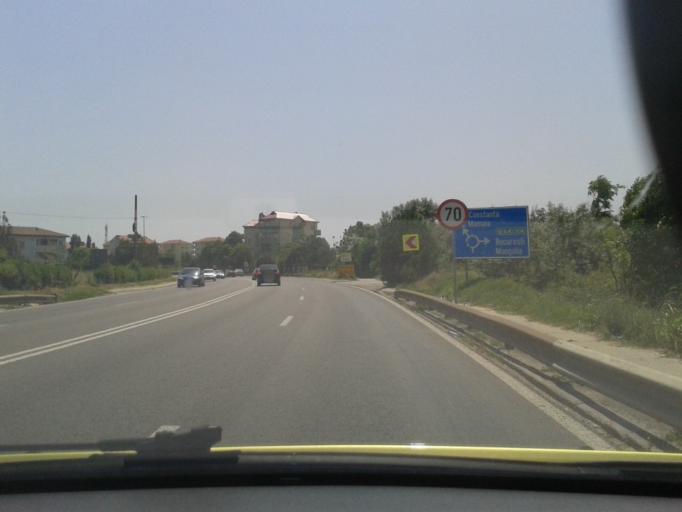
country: RO
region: Constanta
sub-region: Comuna Ovidiu
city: Ovidiu
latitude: 44.2648
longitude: 28.5546
